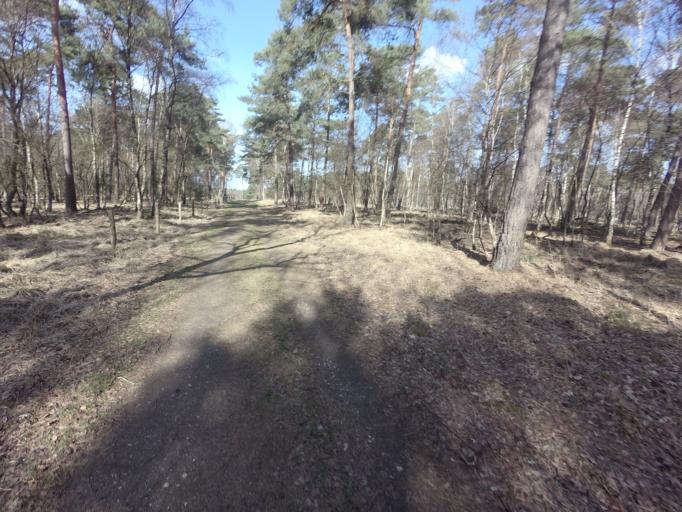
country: DE
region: North Rhine-Westphalia
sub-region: Regierungsbezirk Koln
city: Wassenberg
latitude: 51.1543
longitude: 6.1390
